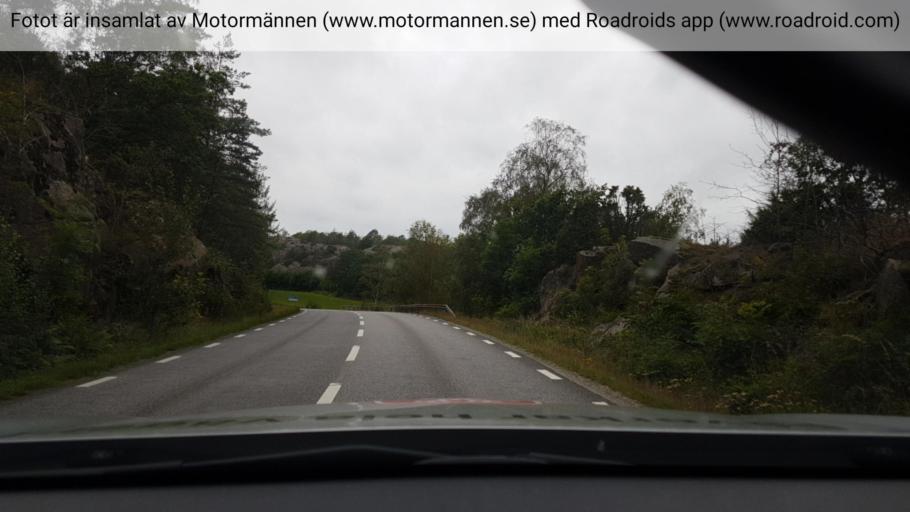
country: SE
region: Vaestra Goetaland
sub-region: Tanums Kommun
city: Grebbestad
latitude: 58.7226
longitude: 11.2850
